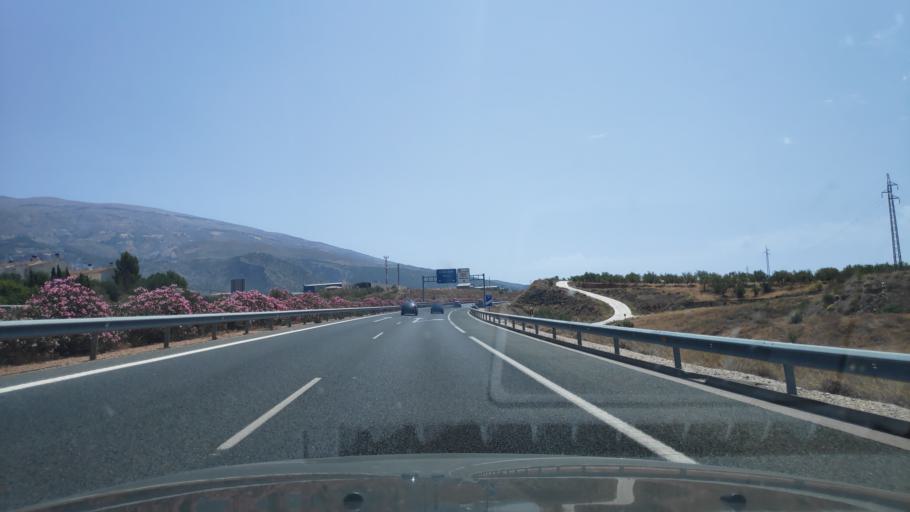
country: ES
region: Andalusia
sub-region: Provincia de Granada
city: Durcal
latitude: 36.9789
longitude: -3.5665
